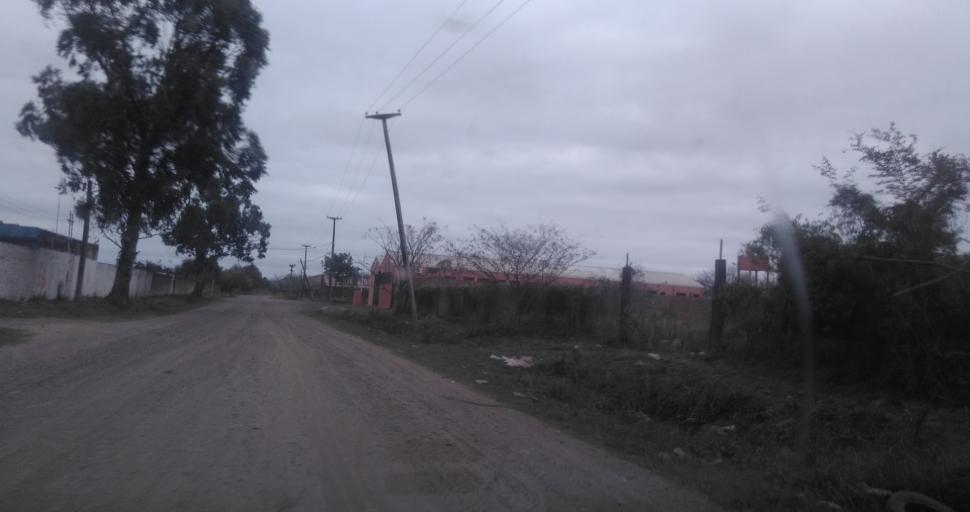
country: AR
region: Chaco
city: Fontana
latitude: -27.4327
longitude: -59.0252
